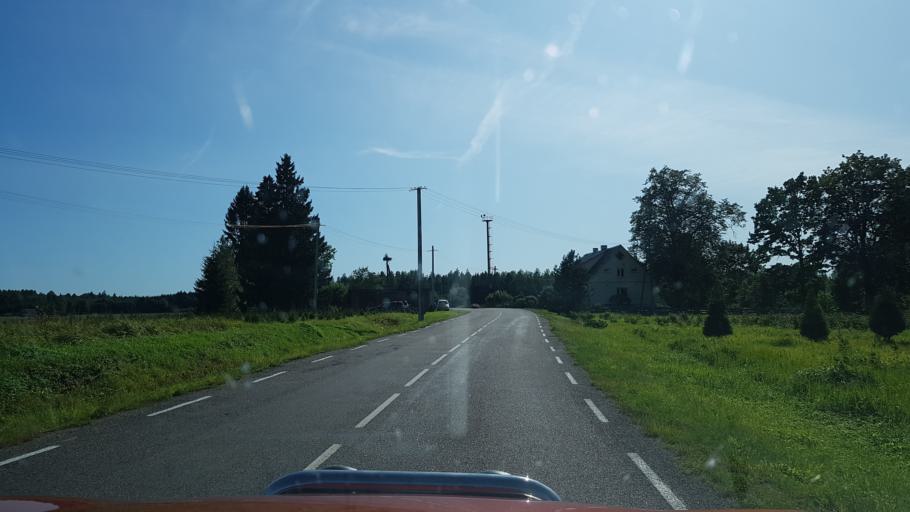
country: EE
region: Paernumaa
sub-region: Saarde vald
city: Kilingi-Nomme
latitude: 58.0220
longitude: 25.0086
